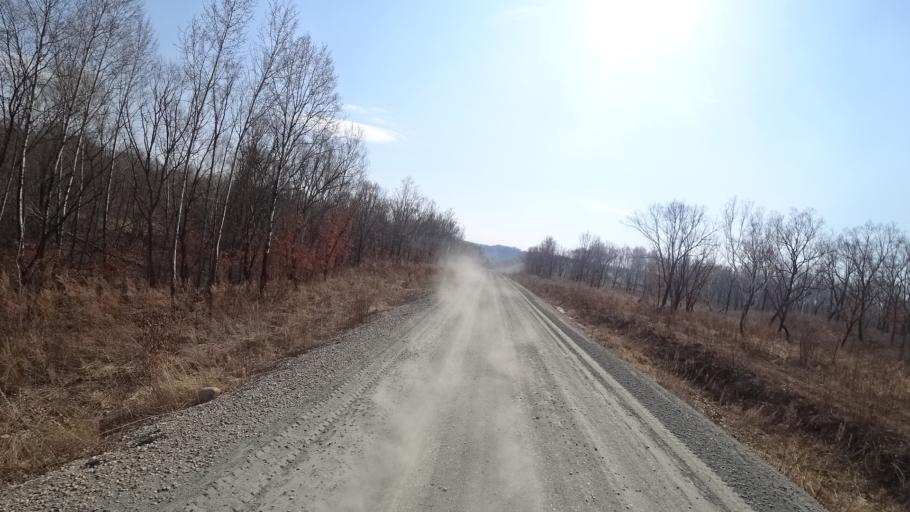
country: RU
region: Amur
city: Novobureyskiy
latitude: 49.8014
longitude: 129.9605
